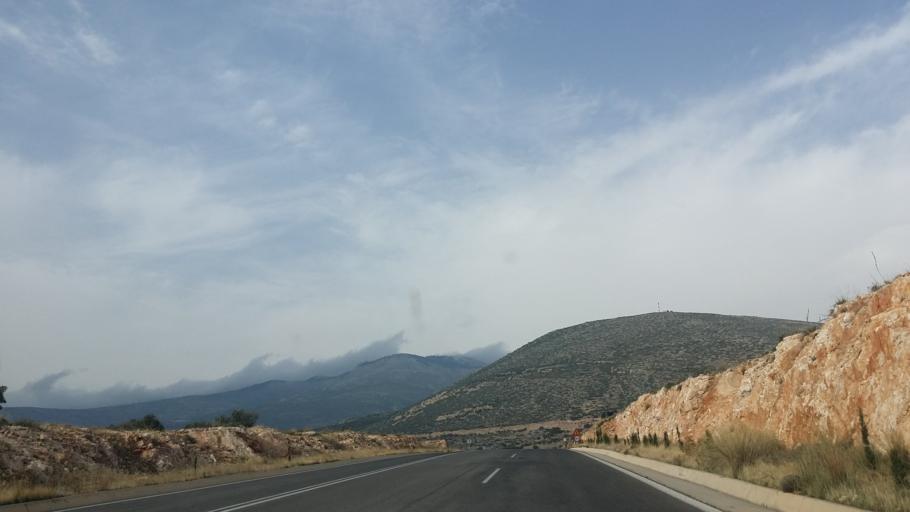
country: GR
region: Central Greece
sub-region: Nomos Voiotias
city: Korini
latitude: 38.2517
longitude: 22.9907
